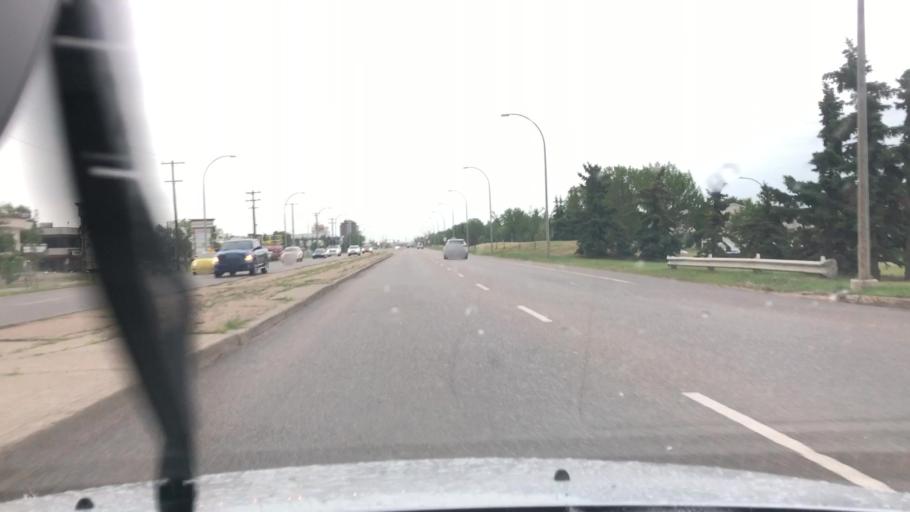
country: CA
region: Alberta
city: St. Albert
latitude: 53.5465
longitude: -113.6127
